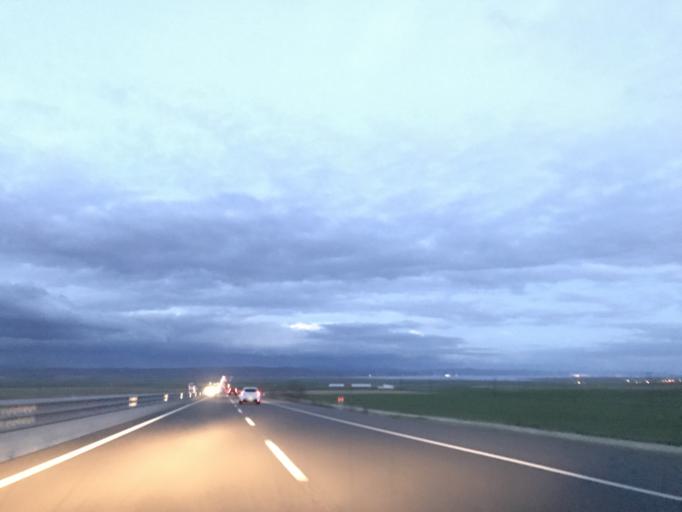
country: TR
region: Konya
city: Kulu
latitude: 39.1554
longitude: 33.2157
